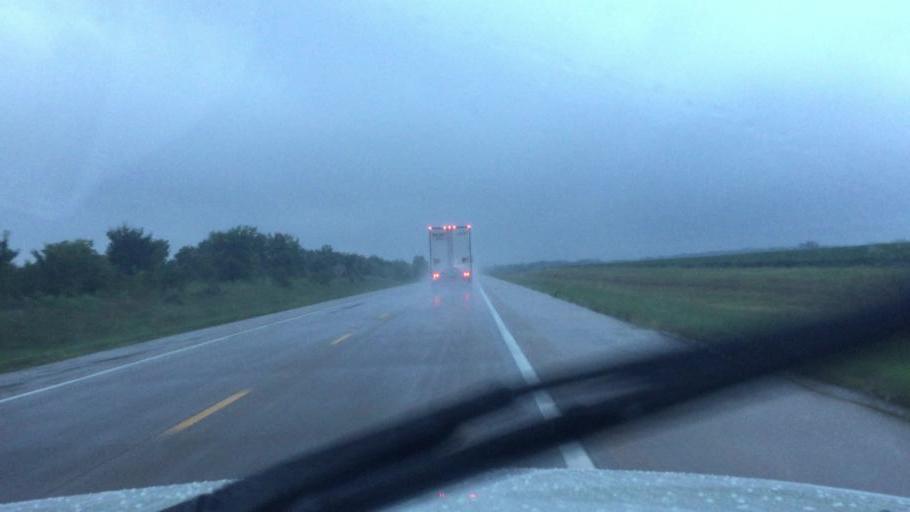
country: US
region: Kansas
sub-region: Neosho County
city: Chanute
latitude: 37.5714
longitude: -95.4709
